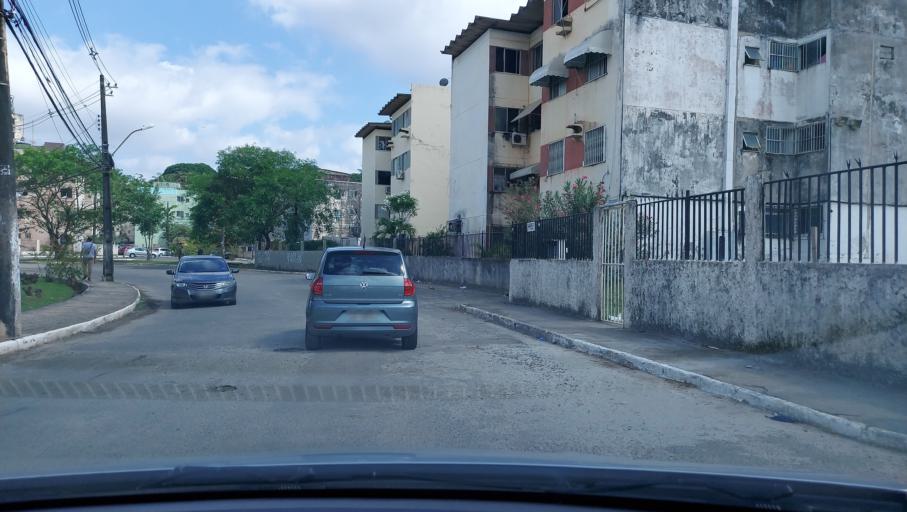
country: BR
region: Bahia
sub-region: Salvador
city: Salvador
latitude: -12.9630
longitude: -38.4298
